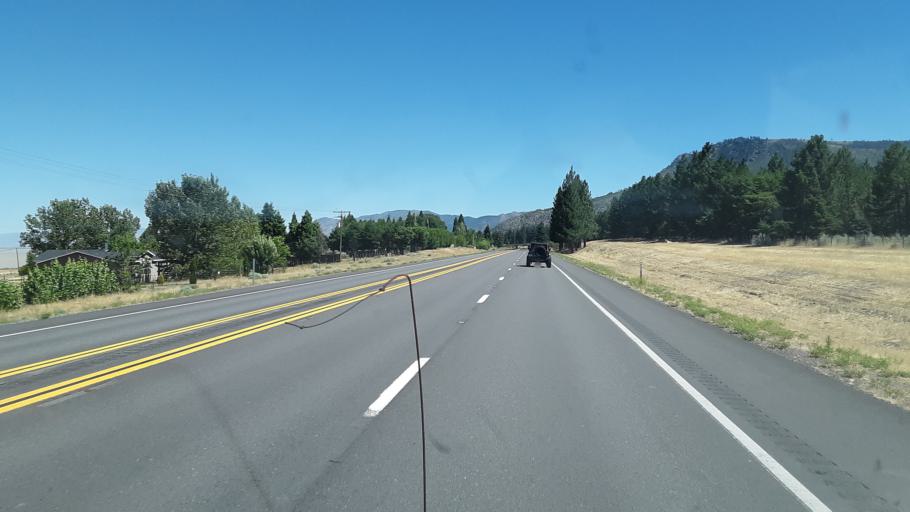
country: US
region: California
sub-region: Lassen County
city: Janesville
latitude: 40.2531
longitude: -120.4639
